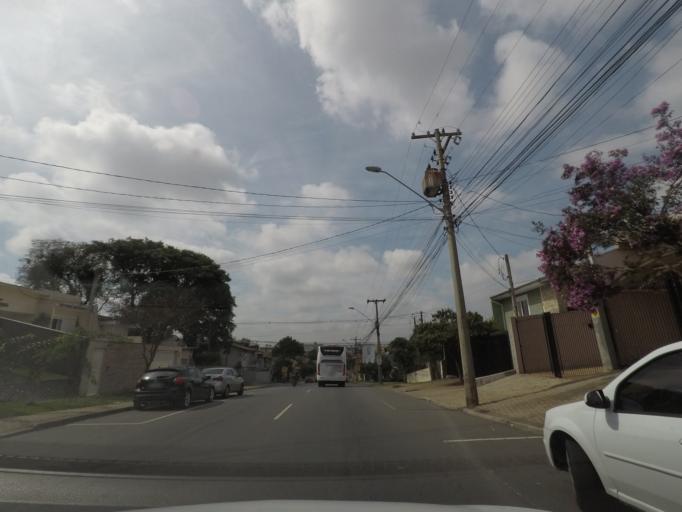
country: BR
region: Parana
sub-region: Curitiba
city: Curitiba
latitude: -25.4795
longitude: -49.3038
